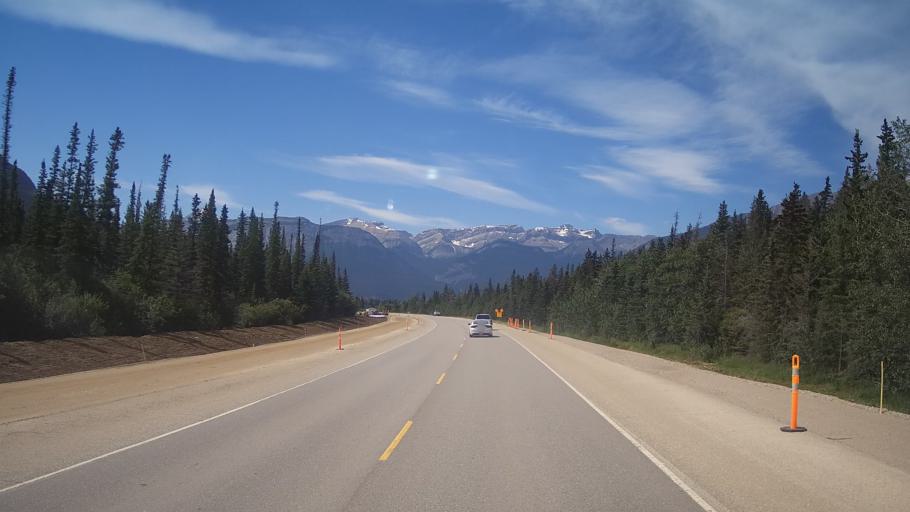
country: CA
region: Alberta
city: Jasper Park Lodge
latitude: 53.0685
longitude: -118.0590
